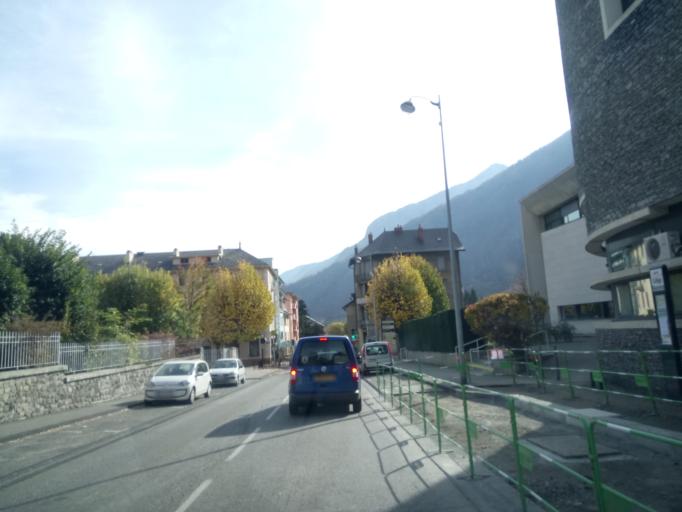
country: FR
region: Rhone-Alpes
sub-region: Departement de la Savoie
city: Saint-Jean-de-Maurienne
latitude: 45.2750
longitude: 6.3471
